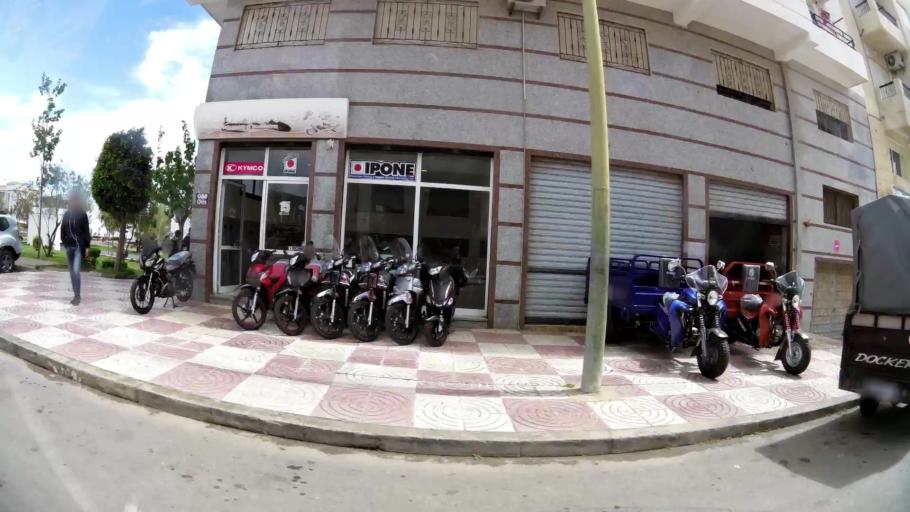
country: MA
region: Tanger-Tetouan
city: Tetouan
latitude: 35.5896
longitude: -5.3356
